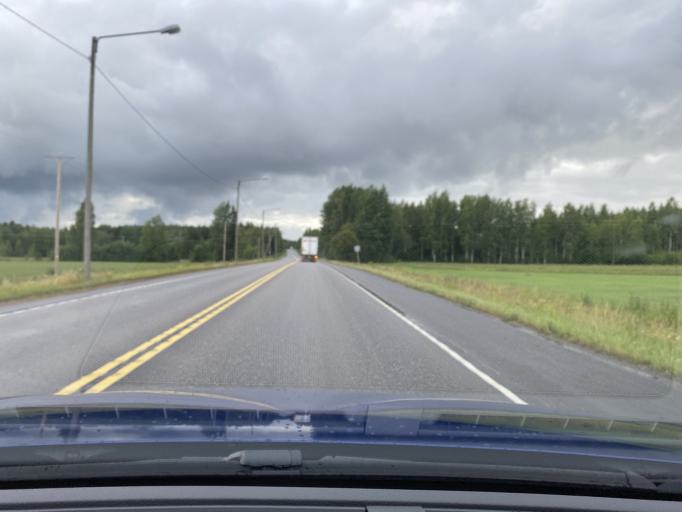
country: FI
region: Uusimaa
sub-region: Helsinki
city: Hyvinge
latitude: 60.5675
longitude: 24.8095
